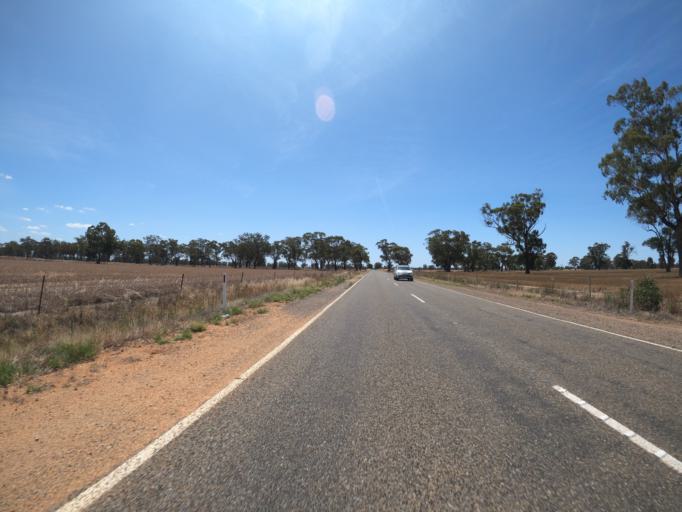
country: AU
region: Victoria
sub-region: Moira
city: Yarrawonga
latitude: -36.1808
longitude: 145.9672
